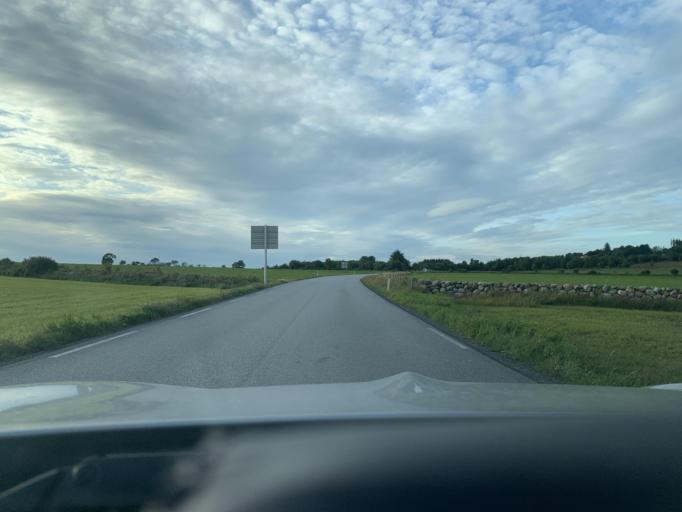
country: NO
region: Rogaland
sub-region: Time
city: Bryne
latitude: 58.6946
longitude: 5.7102
